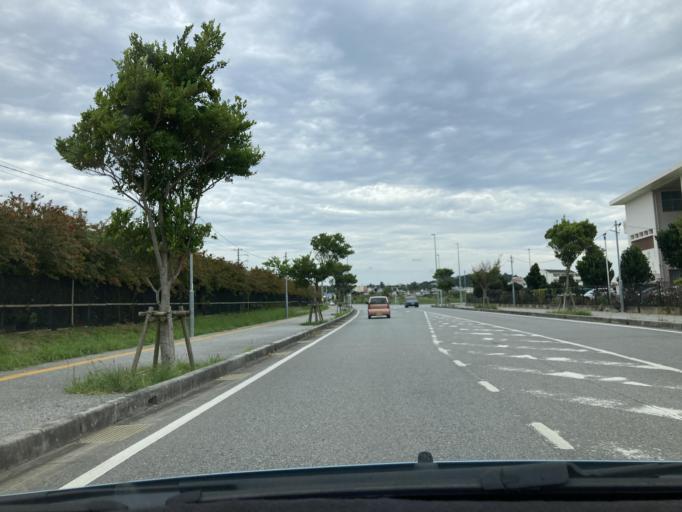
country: JP
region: Okinawa
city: Ishikawa
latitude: 26.3957
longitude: 127.7410
